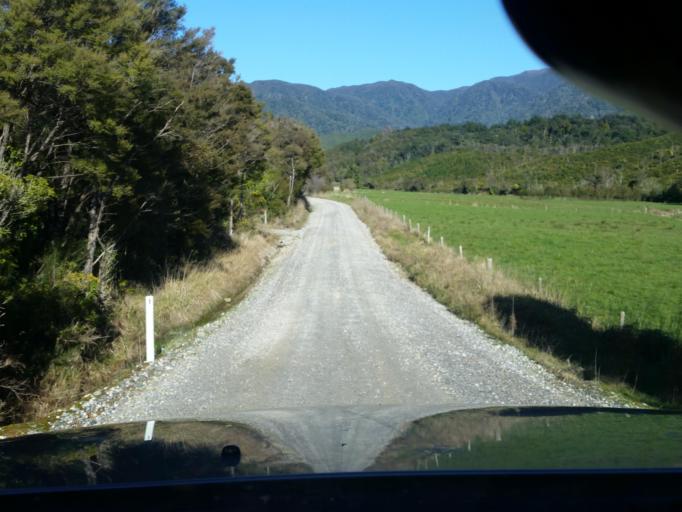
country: NZ
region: Tasman
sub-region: Tasman District
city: Takaka
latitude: -40.7930
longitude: 172.7315
